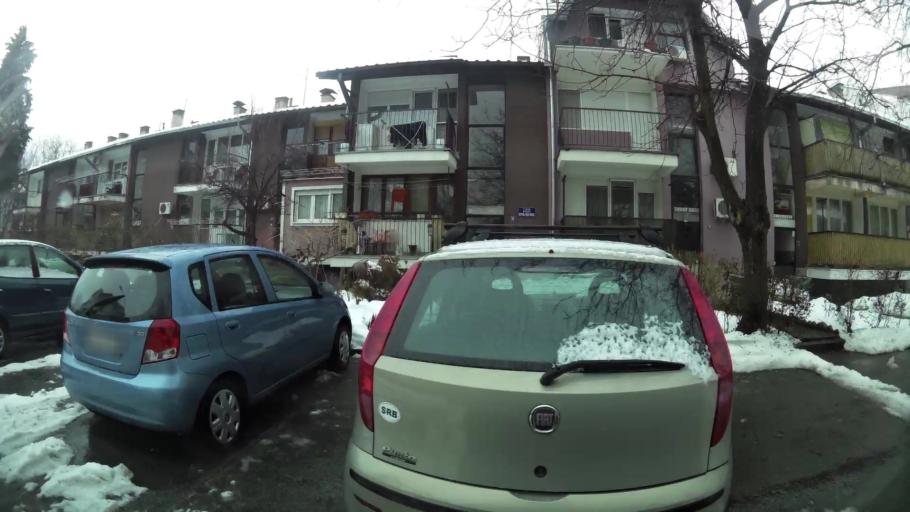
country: RS
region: Central Serbia
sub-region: Belgrade
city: Zemun
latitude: 44.8714
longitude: 20.3210
